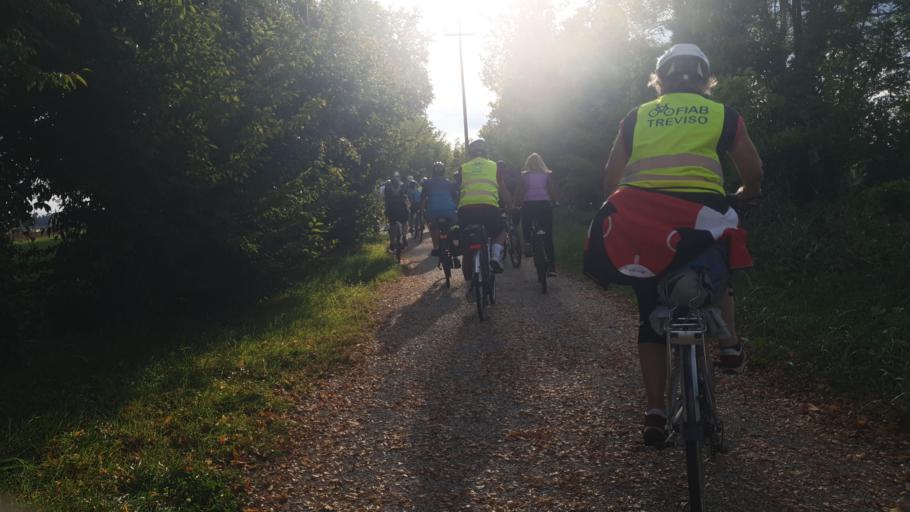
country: IT
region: Veneto
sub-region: Provincia di Padova
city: Montagnana
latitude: 45.2494
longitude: 11.4754
